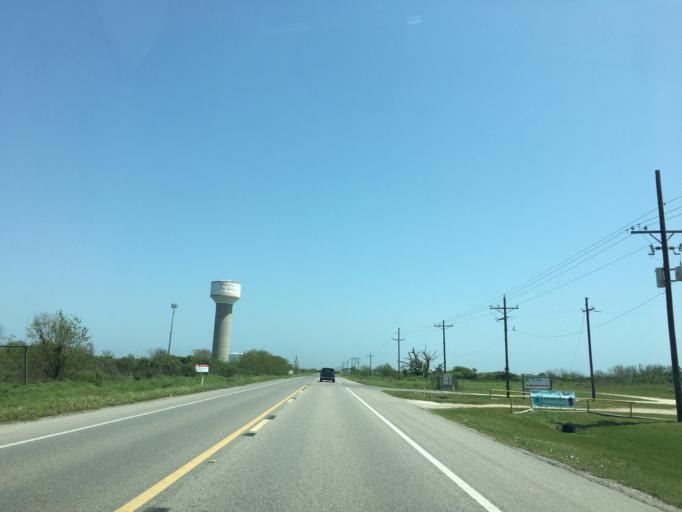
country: US
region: Texas
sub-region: Galveston County
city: Bolivar Peninsula
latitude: 29.4199
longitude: -94.7045
